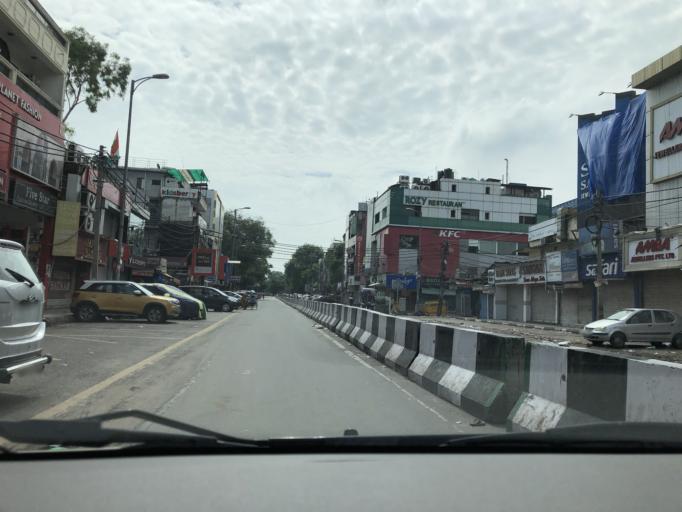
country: IN
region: NCT
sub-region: New Delhi
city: New Delhi
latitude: 28.5697
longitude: 77.2421
